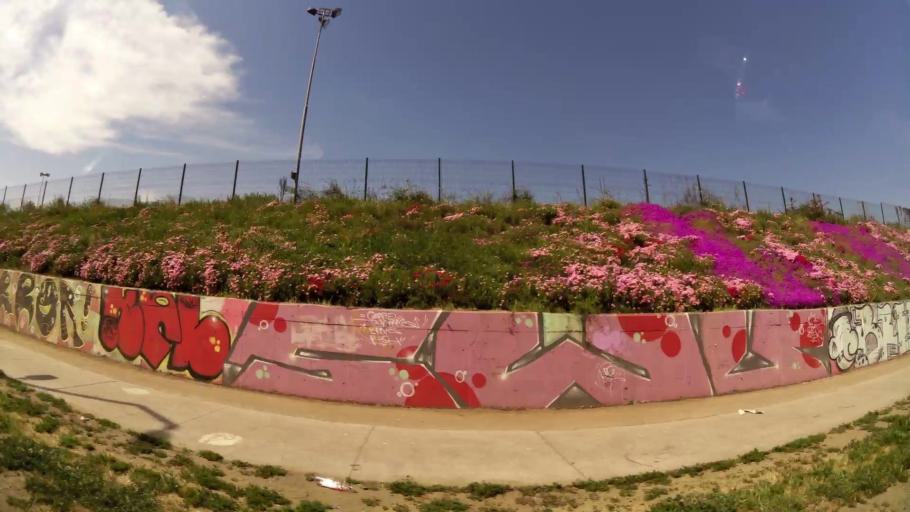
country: CL
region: Santiago Metropolitan
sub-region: Provincia de Santiago
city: Villa Presidente Frei, Nunoa, Santiago, Chile
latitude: -33.4650
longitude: -70.5485
